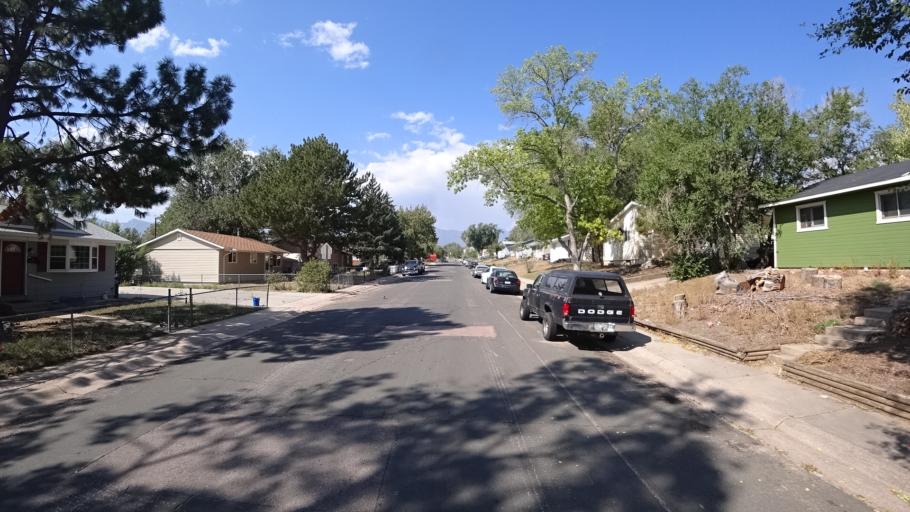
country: US
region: Colorado
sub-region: El Paso County
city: Colorado Springs
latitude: 38.8212
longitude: -104.7903
